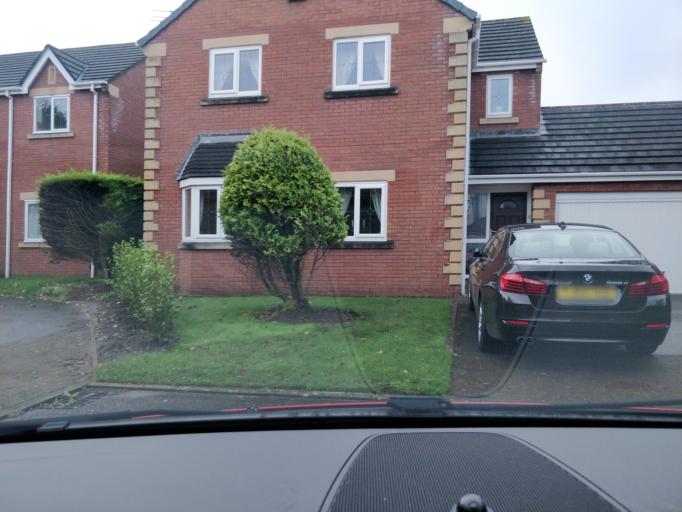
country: GB
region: England
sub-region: Sefton
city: Southport
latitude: 53.6321
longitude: -3.0238
